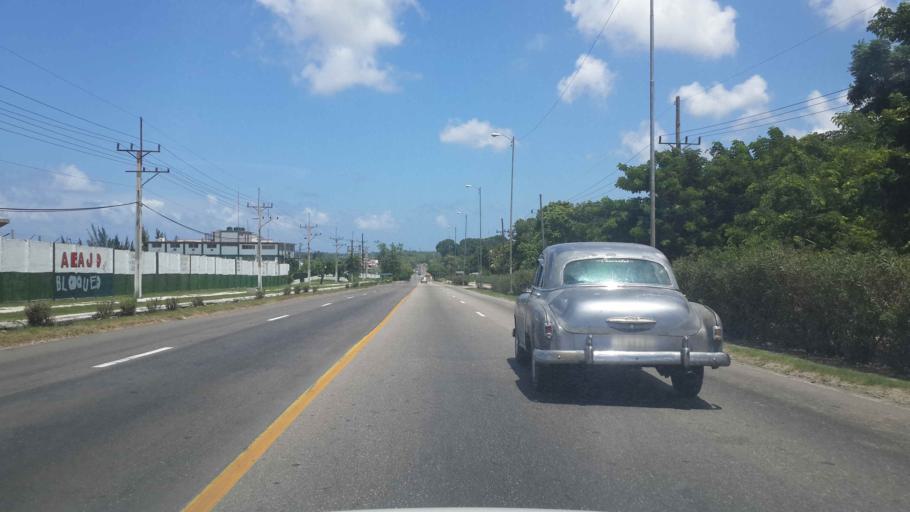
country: CU
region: La Habana
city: Regla
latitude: 23.1271
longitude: -82.3171
